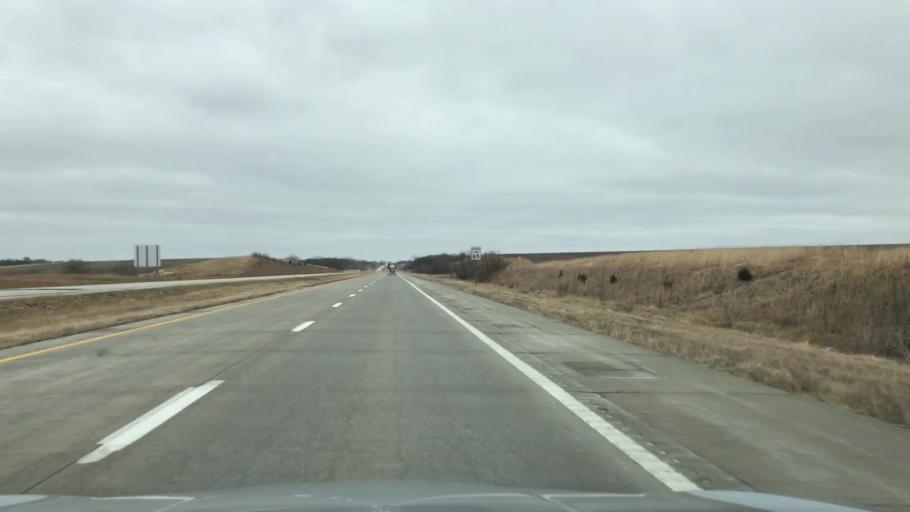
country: US
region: Missouri
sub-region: Caldwell County
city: Hamilton
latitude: 39.7338
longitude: -93.9824
